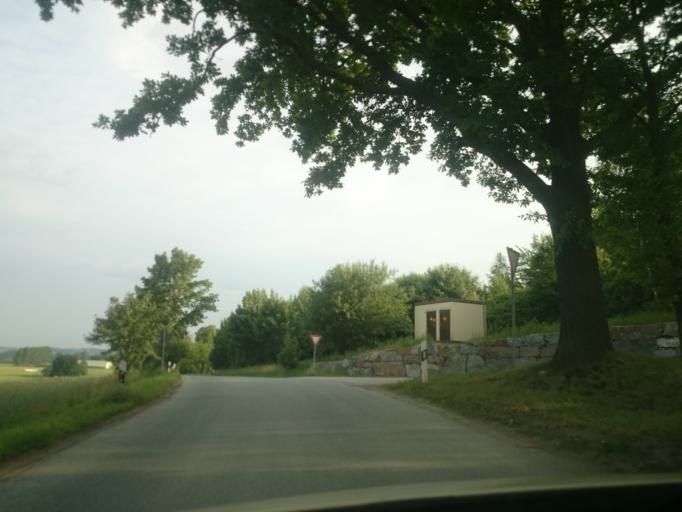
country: DE
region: Saxony
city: Borstendorf
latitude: 50.7874
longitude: 13.1719
